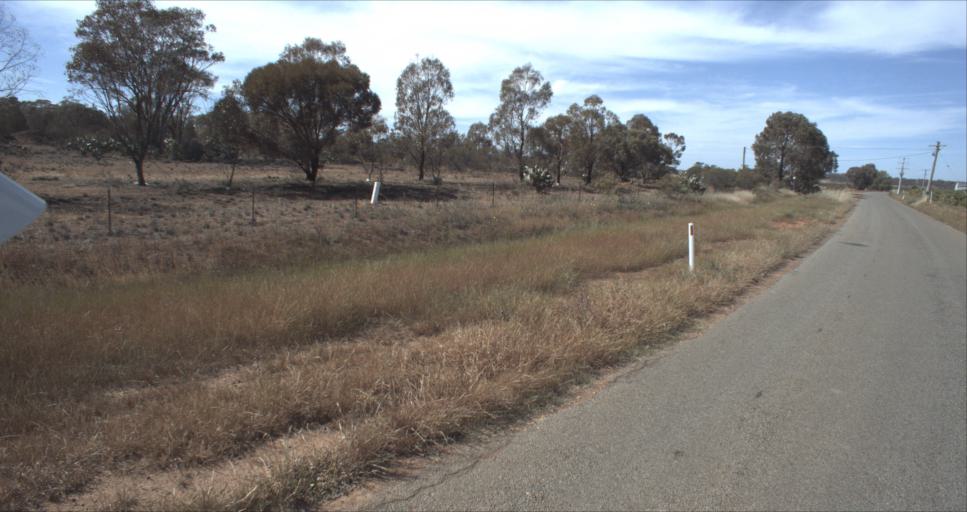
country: AU
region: New South Wales
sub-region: Leeton
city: Leeton
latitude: -34.5801
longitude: 146.4774
